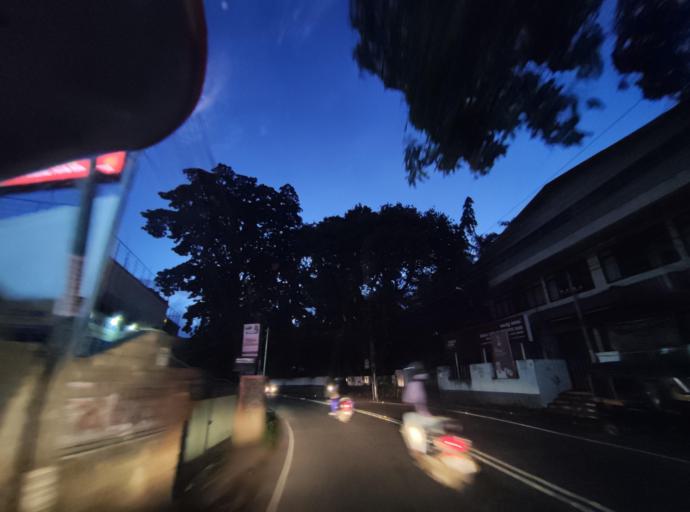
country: IN
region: Kerala
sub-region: Thiruvananthapuram
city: Thiruvananthapuram
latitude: 8.5388
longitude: 76.9651
